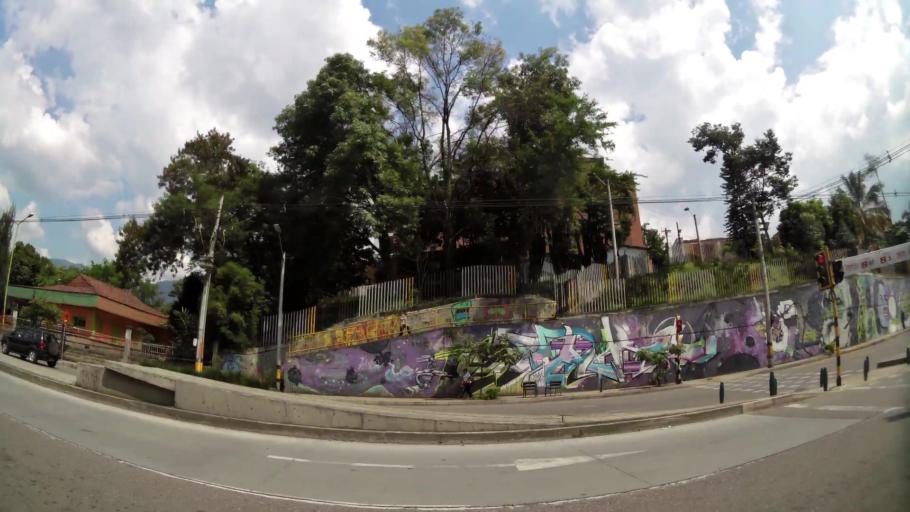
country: CO
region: Antioquia
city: Envigado
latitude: 6.1681
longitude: -75.5902
